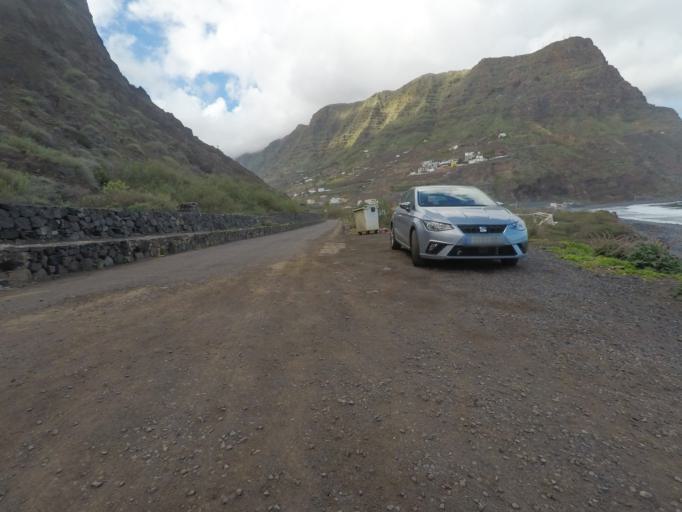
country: ES
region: Canary Islands
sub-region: Provincia de Santa Cruz de Tenerife
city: Hermigua
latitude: 28.1773
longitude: -17.1773
